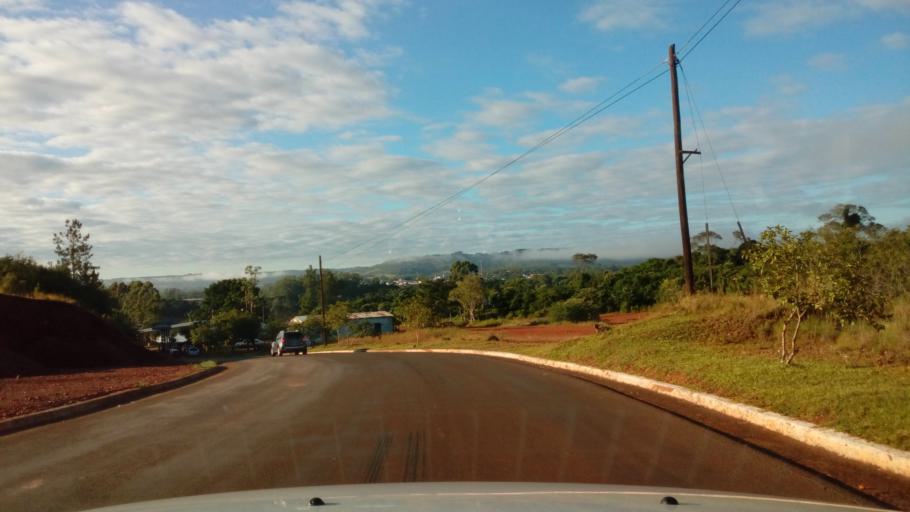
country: AR
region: Misiones
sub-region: Departamento de San Javier
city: San Javier
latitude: -27.8905
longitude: -55.1357
